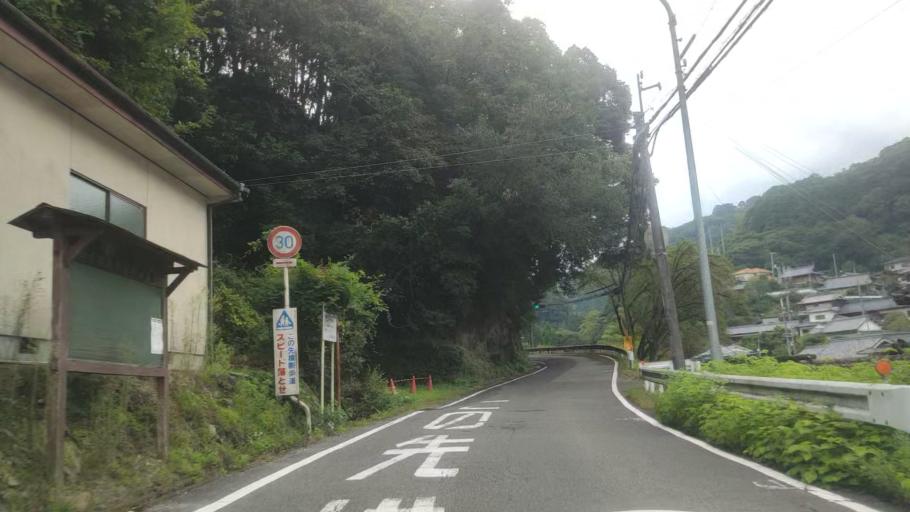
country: JP
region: Wakayama
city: Hashimoto
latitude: 34.2684
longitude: 135.5542
